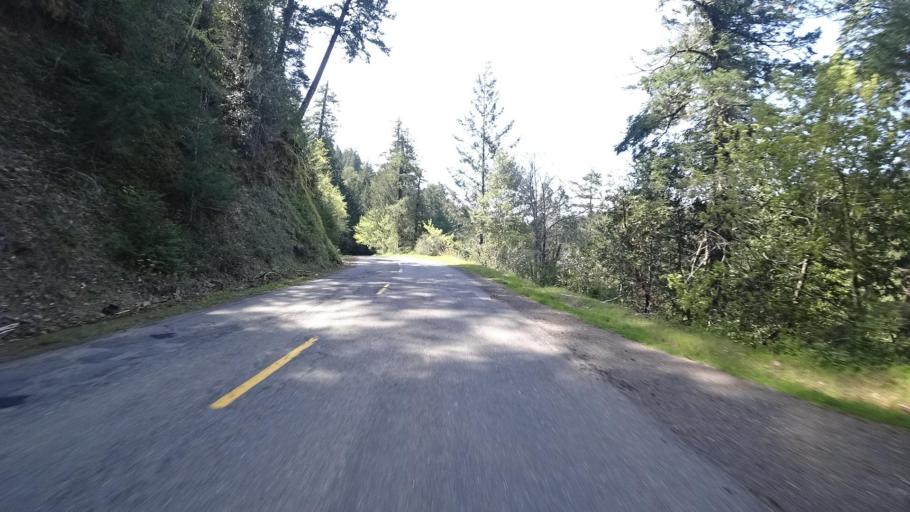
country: US
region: California
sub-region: Humboldt County
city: Redway
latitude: 40.3326
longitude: -123.6755
